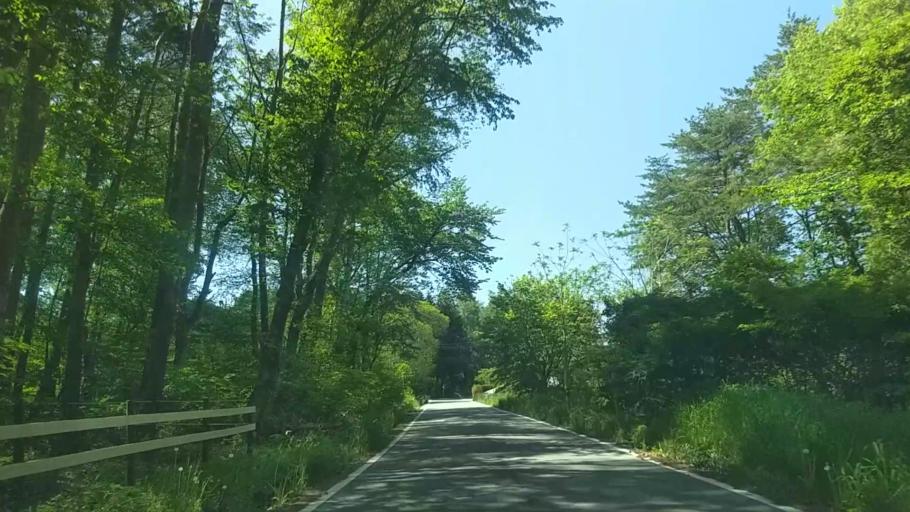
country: JP
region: Yamanashi
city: Nirasaki
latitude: 35.9016
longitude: 138.4480
